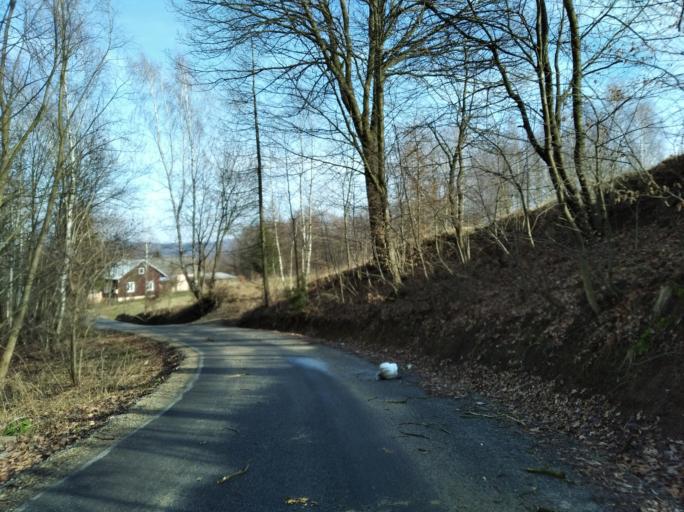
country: PL
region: Subcarpathian Voivodeship
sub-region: Powiat brzozowski
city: Gorki
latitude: 49.6441
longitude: 22.0574
